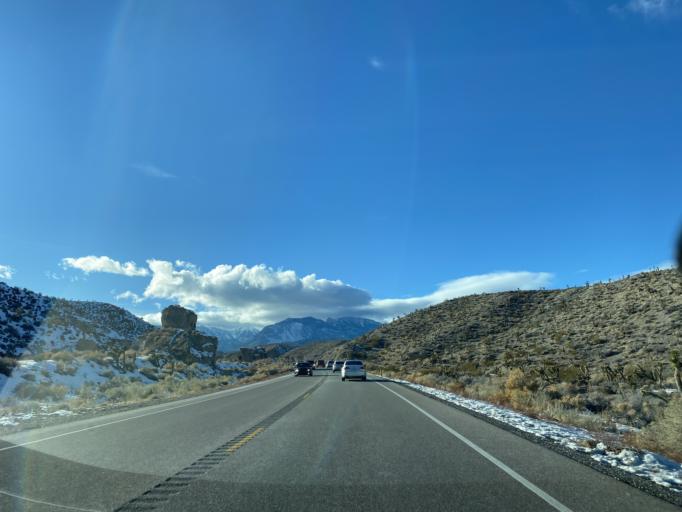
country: US
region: Nevada
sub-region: Clark County
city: Summerlin South
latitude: 36.2773
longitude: -115.4825
